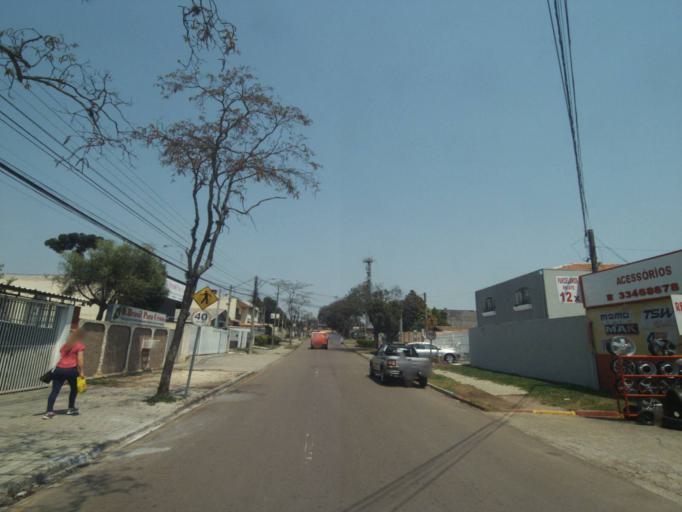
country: BR
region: Parana
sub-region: Sao Jose Dos Pinhais
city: Sao Jose dos Pinhais
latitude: -25.5130
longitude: -49.2735
